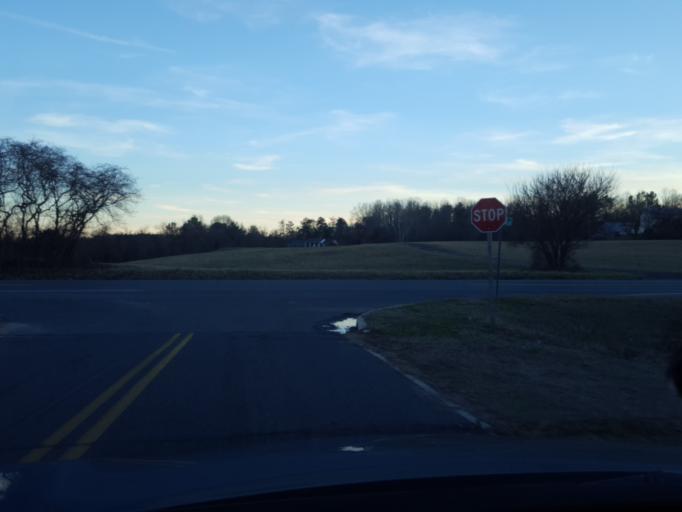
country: US
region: Maryland
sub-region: Saint Mary's County
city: Golden Beach
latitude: 38.5150
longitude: -76.6972
